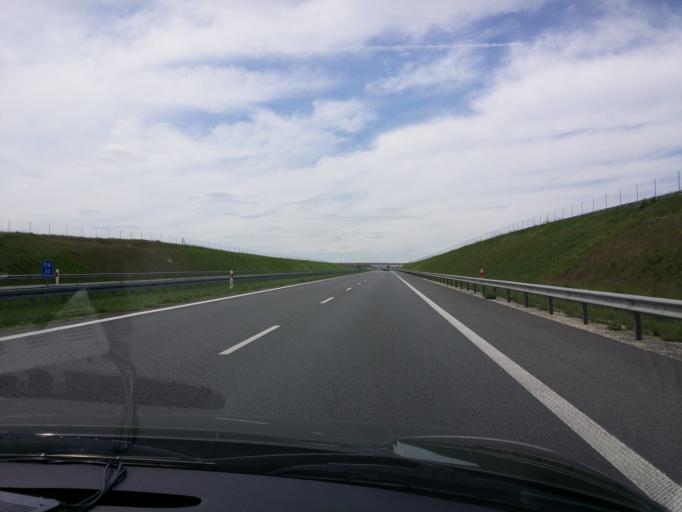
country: PL
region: Masovian Voivodeship
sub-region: Powiat szydlowiecki
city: Jastrzab
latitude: 51.2700
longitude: 20.9407
